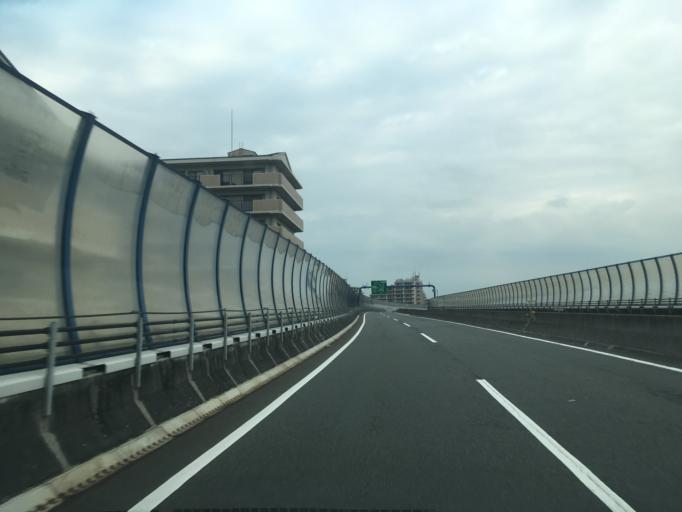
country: JP
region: Kanagawa
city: Chigasaki
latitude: 35.3312
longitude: 139.3829
